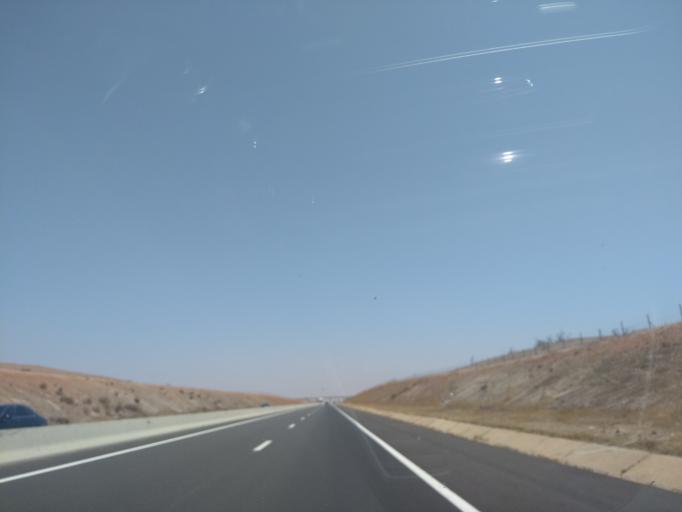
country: MA
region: Marrakech-Tensift-Al Haouz
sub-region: Kelaa-Des-Sraghna
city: Sidi Abdallah
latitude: 32.3136
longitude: -7.9589
